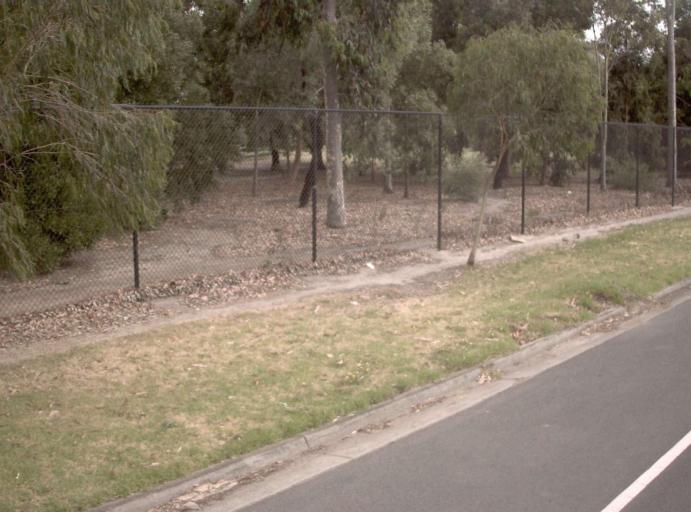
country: AU
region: Victoria
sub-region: Monash
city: Oakleigh South
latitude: -37.9230
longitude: 145.1013
